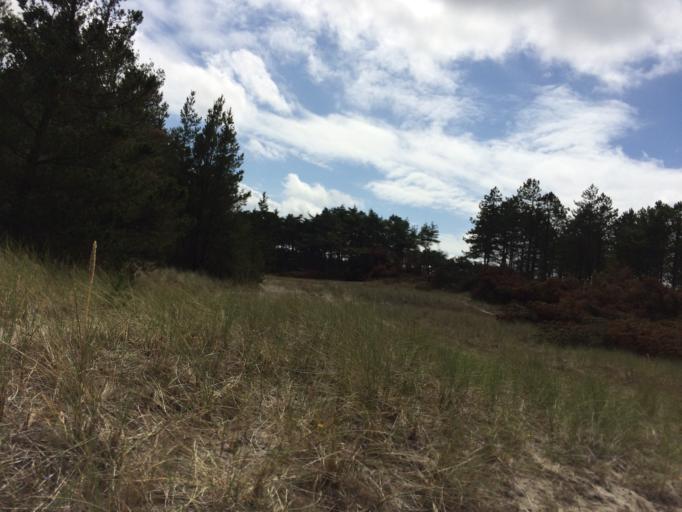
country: DK
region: Central Jutland
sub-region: Holstebro Kommune
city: Ulfborg
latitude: 56.2940
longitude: 8.1503
